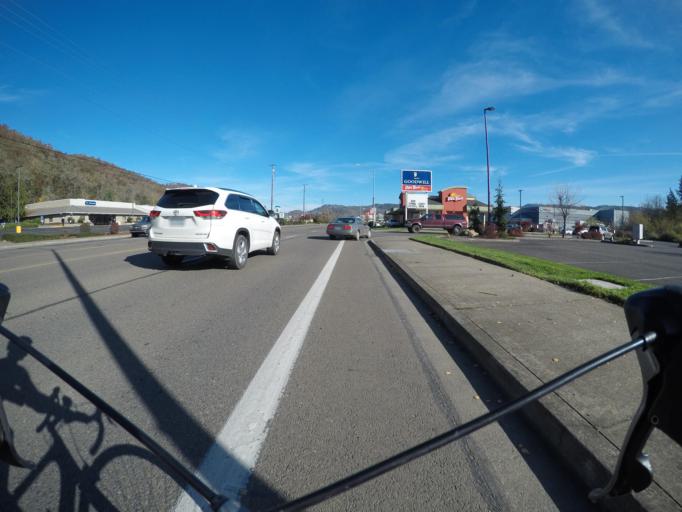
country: US
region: Oregon
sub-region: Douglas County
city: Roseburg
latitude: 43.2367
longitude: -123.3716
